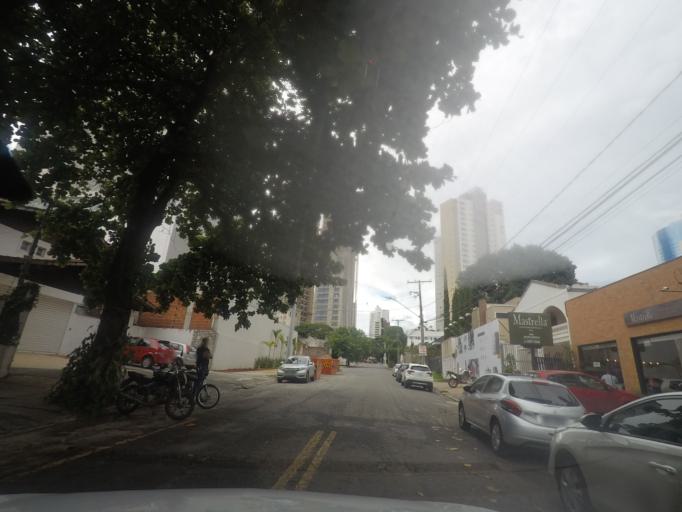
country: BR
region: Goias
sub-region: Goiania
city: Goiania
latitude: -16.6939
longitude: -49.2674
